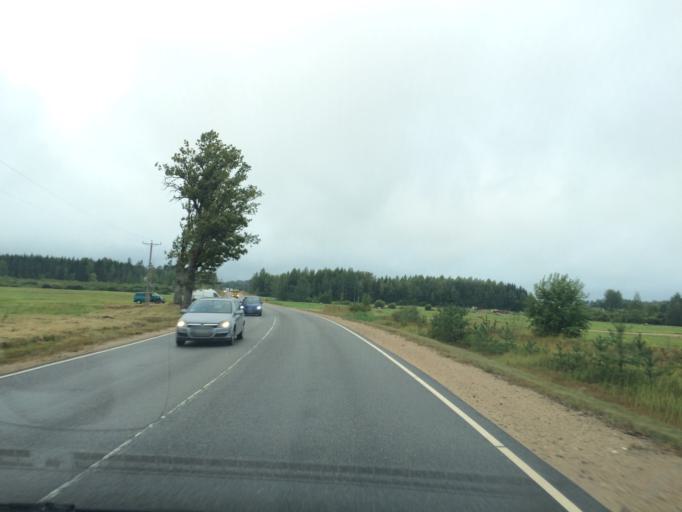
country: LV
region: Ogre
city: Ogre
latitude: 56.8596
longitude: 24.6263
